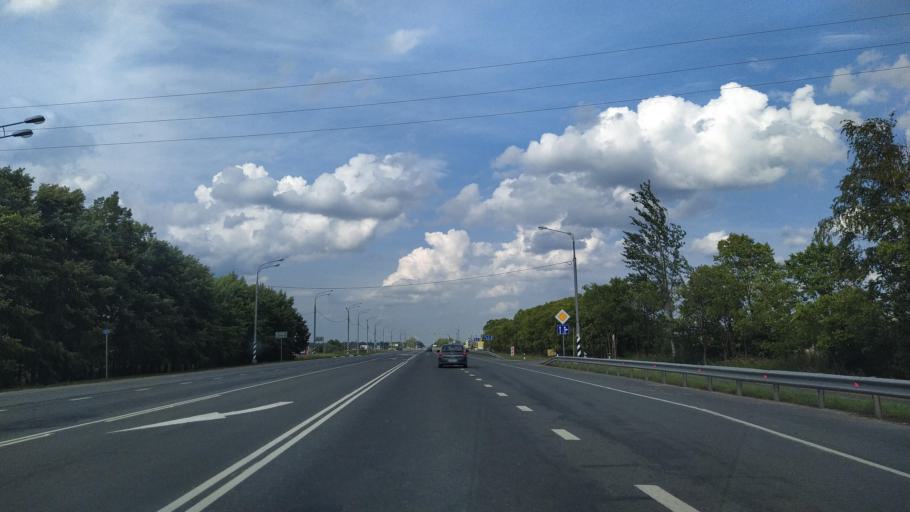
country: RU
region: Novgorod
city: Shimsk
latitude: 58.2177
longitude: 30.7344
